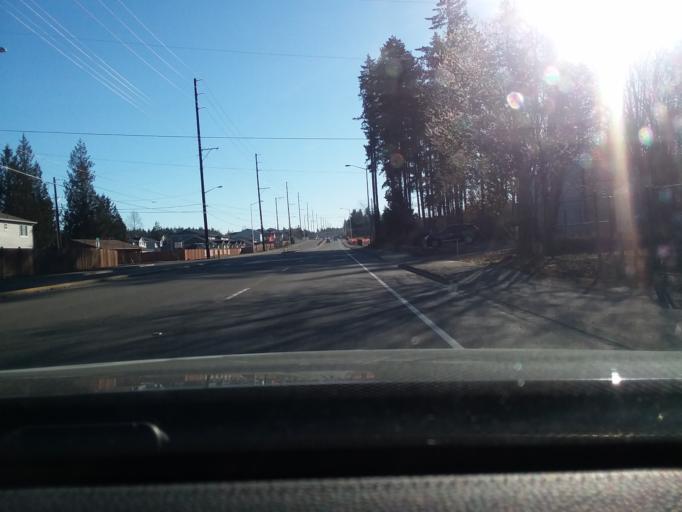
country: US
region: Washington
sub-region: Pierce County
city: Frederickson
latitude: 47.0964
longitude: -122.3214
